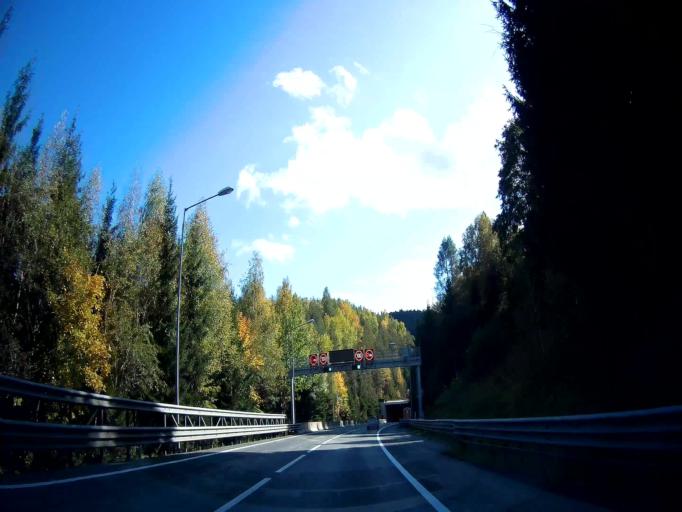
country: AT
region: Carinthia
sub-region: Politischer Bezirk Spittal an der Drau
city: Seeboden
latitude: 46.8062
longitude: 13.5197
